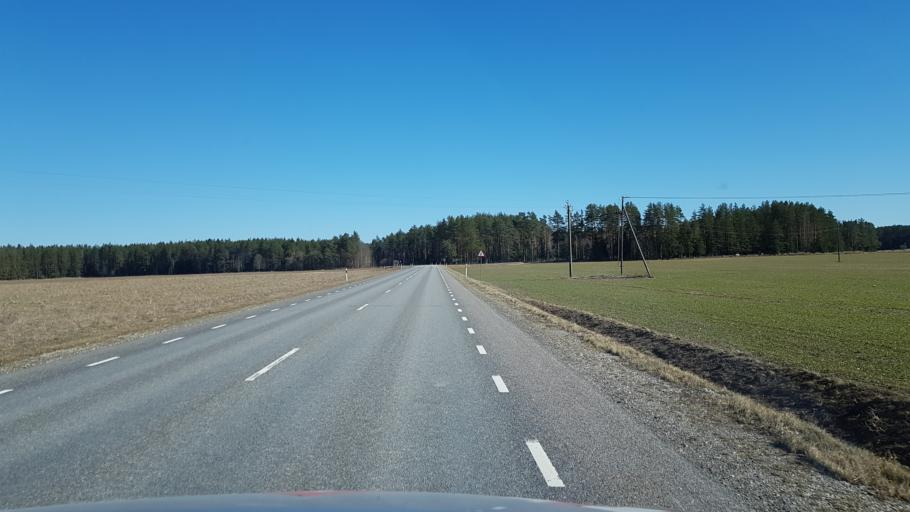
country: EE
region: Laeaene-Virumaa
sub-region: Viru-Nigula vald
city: Kunda
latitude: 59.3624
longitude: 26.6192
